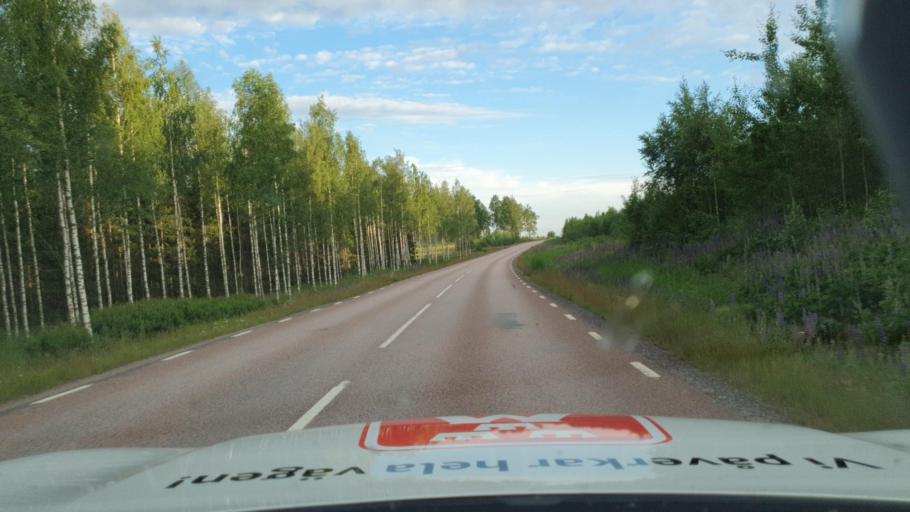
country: SE
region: Vaermland
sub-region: Karlstads Kommun
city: Molkom
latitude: 59.4827
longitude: 13.8104
